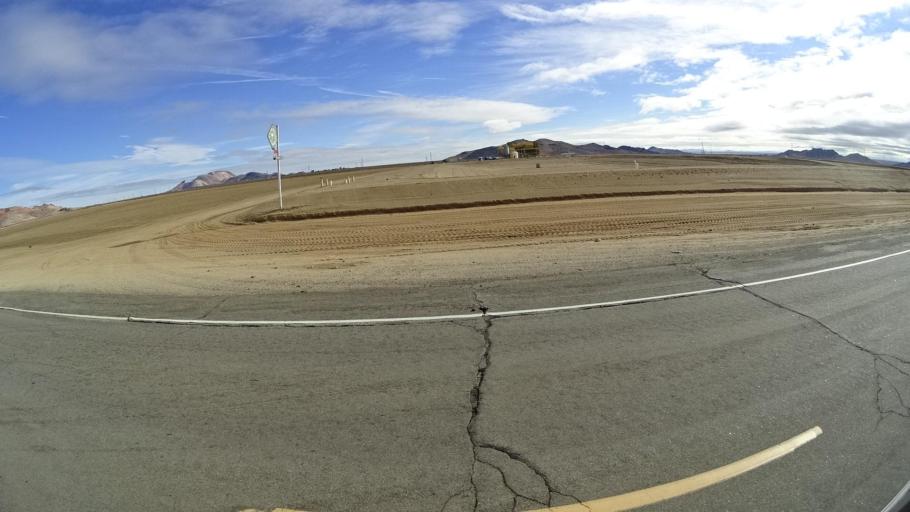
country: US
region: California
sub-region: Kern County
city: Rosamond
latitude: 34.9291
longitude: -118.2916
